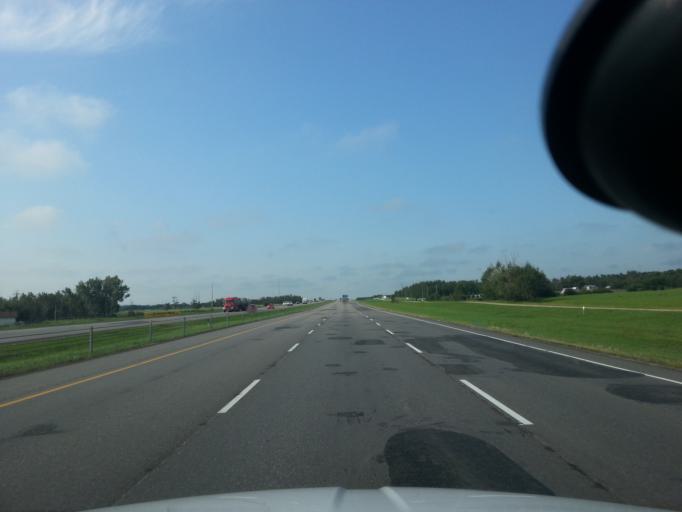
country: CA
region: Alberta
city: Penhold
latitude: 52.0801
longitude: -113.8635
